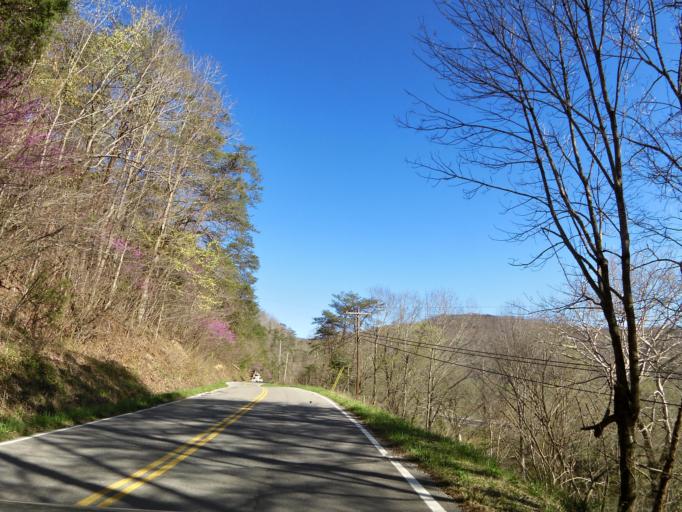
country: US
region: Tennessee
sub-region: Scott County
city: Huntsville
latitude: 36.3302
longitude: -84.3770
